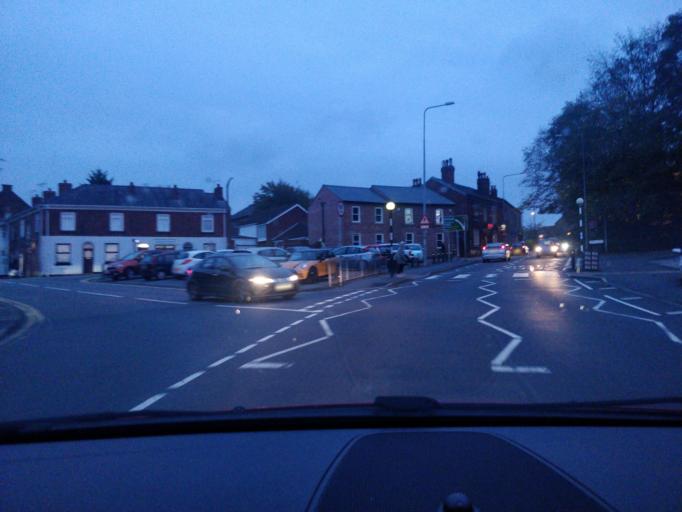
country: GB
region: England
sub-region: Lancashire
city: Ormskirk
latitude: 53.5701
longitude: -2.8881
